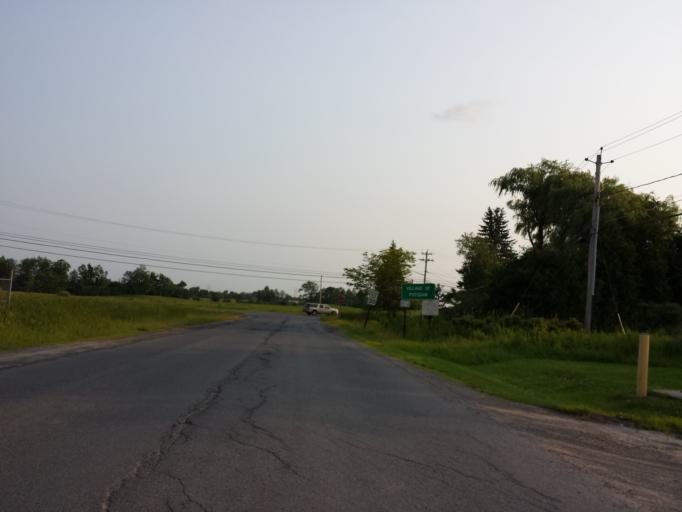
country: US
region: New York
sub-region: St. Lawrence County
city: Potsdam
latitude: 44.6707
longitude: -74.9575
